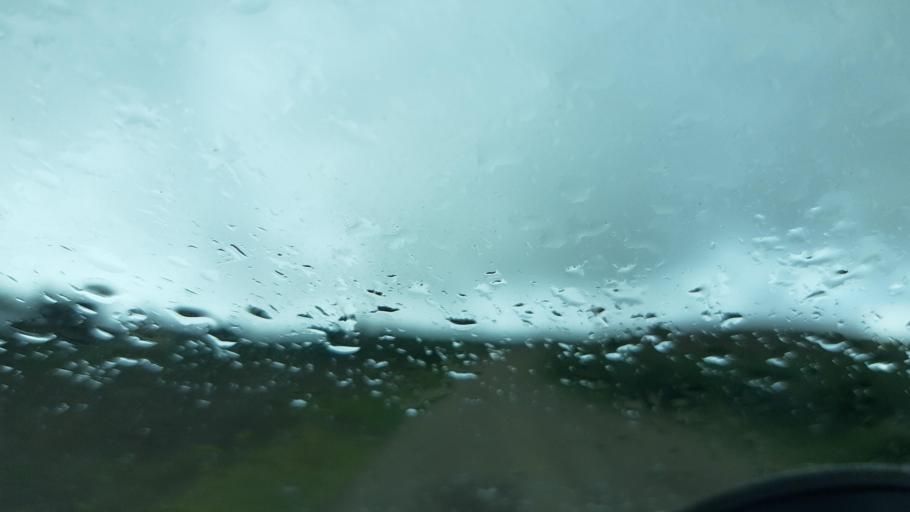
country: CO
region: Boyaca
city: Cucaita
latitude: 5.5204
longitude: -73.4410
